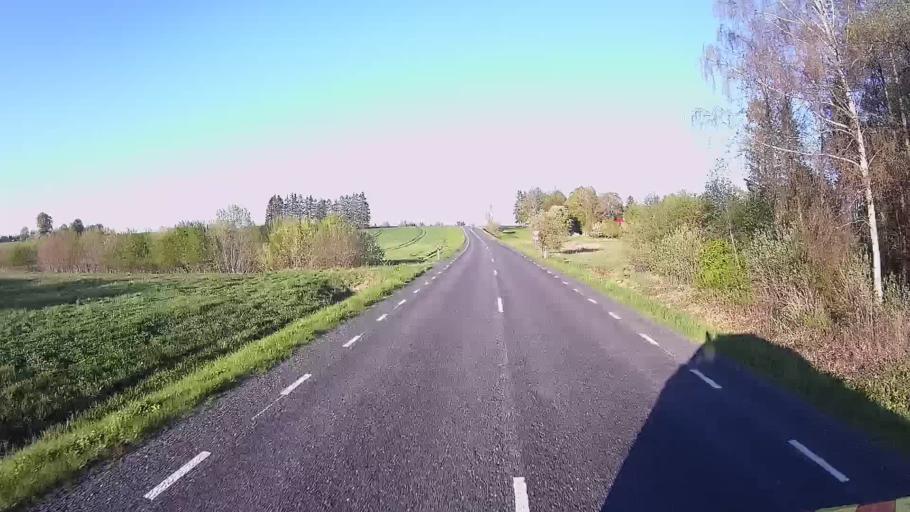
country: EE
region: Jogevamaa
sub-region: Poltsamaa linn
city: Poltsamaa
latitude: 58.5218
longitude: 25.9824
